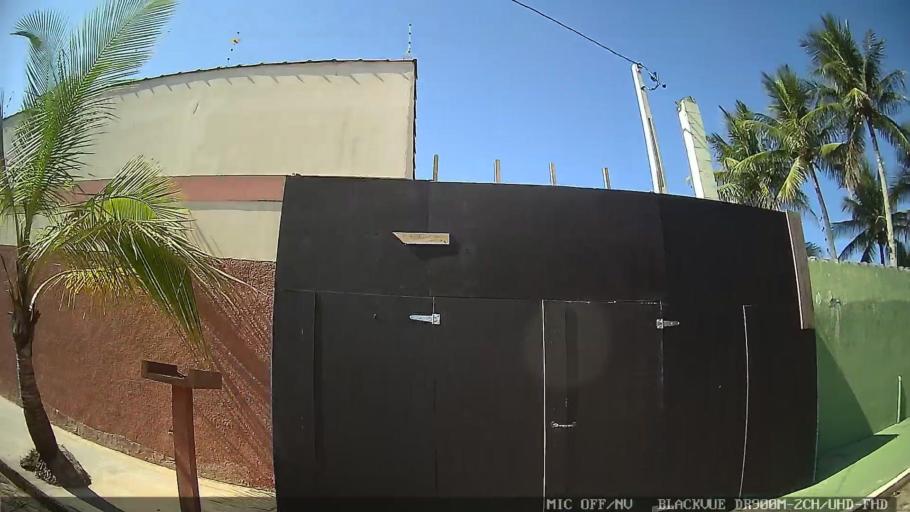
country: BR
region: Sao Paulo
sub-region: Peruibe
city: Peruibe
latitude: -24.2949
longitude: -46.9637
